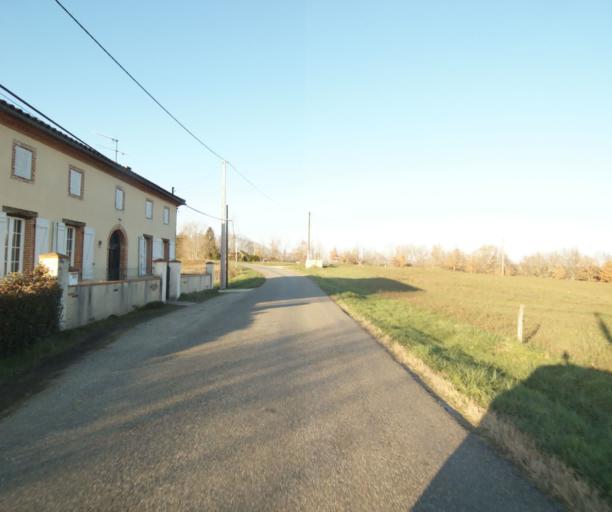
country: FR
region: Midi-Pyrenees
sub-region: Departement du Tarn-et-Garonne
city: Moissac
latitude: 44.1351
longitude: 1.1243
